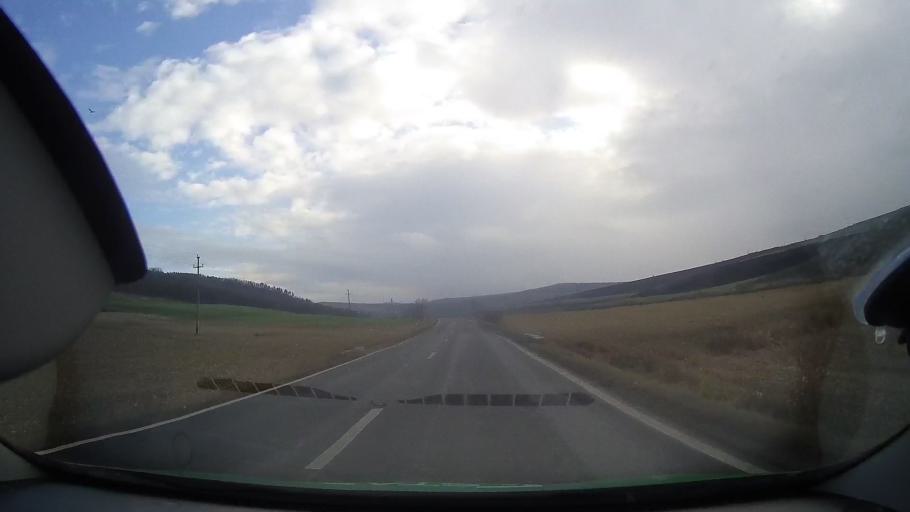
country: RO
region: Mures
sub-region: Comuna Cucerdea
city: Cucerdea
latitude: 46.3745
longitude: 24.2582
